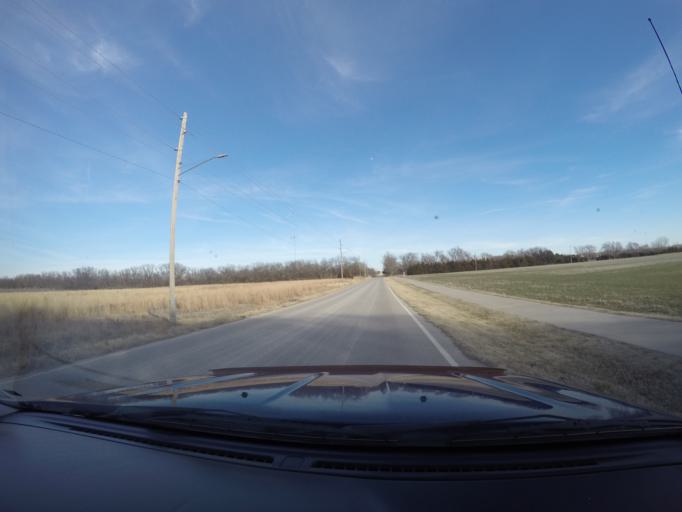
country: US
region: Kansas
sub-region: Harvey County
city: North Newton
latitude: 38.0718
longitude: -97.3390
